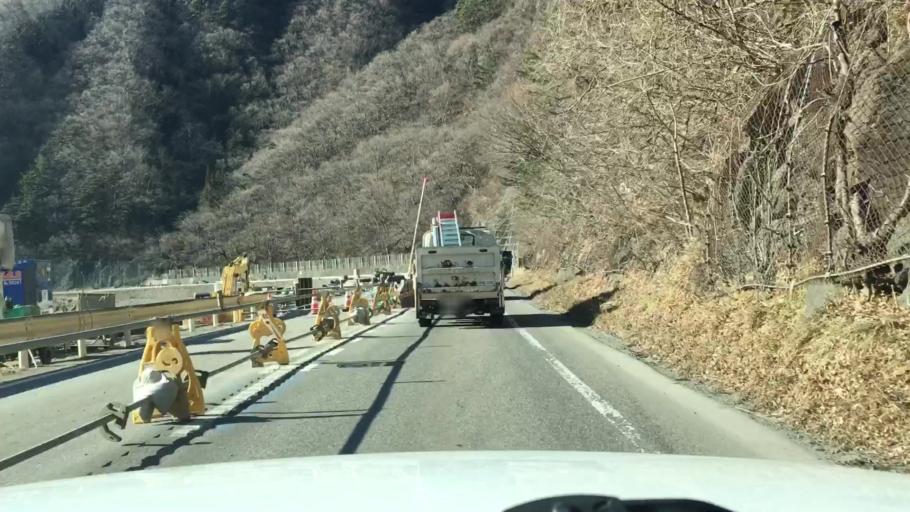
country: JP
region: Iwate
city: Miyako
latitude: 39.6276
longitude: 141.8136
